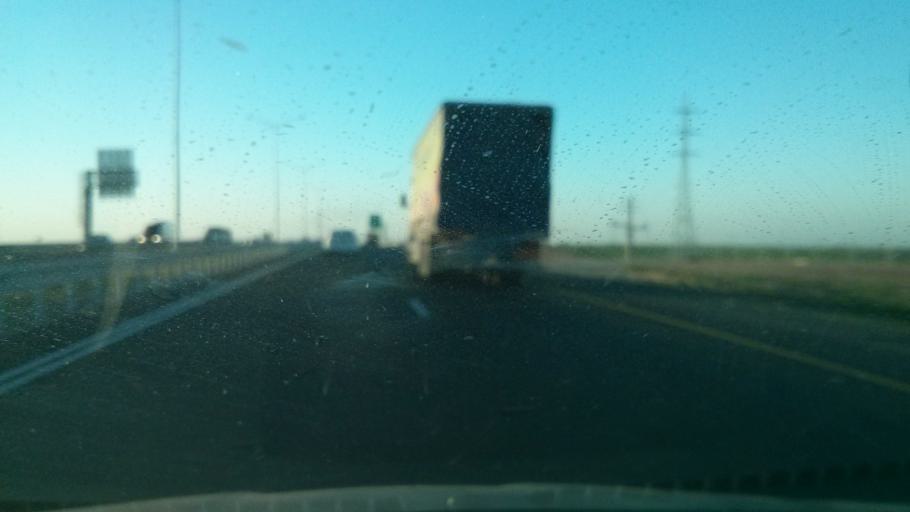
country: IL
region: Southern District
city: Lehavim
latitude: 31.4302
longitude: 34.7794
